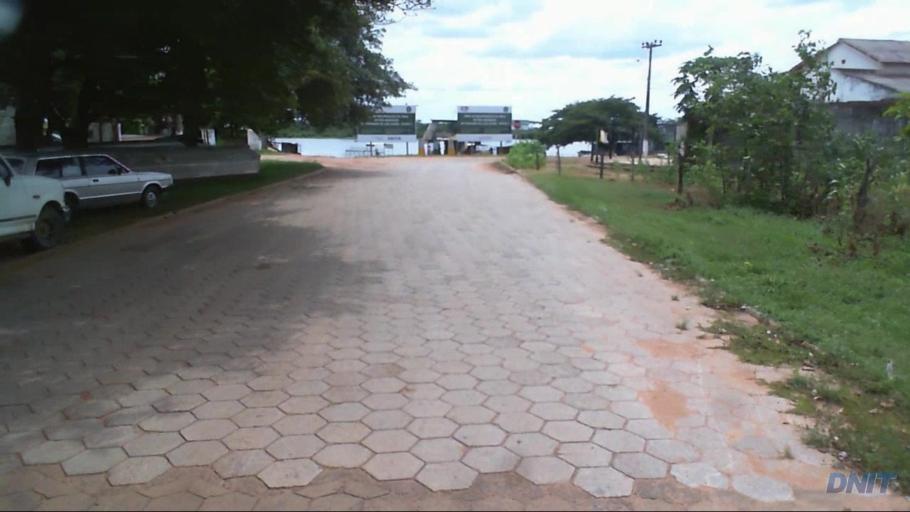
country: BR
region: Goias
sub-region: Sao Miguel Do Araguaia
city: Sao Miguel do Araguaia
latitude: -13.2186
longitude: -50.5749
